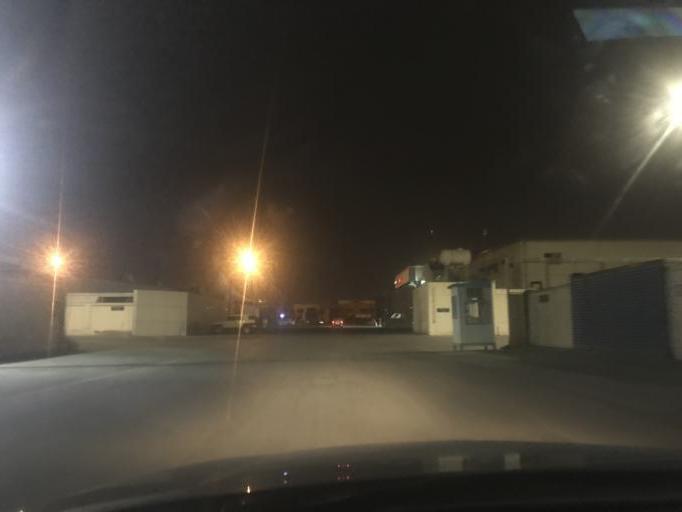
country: SA
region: Ar Riyad
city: Riyadh
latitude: 24.7254
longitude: 46.7827
